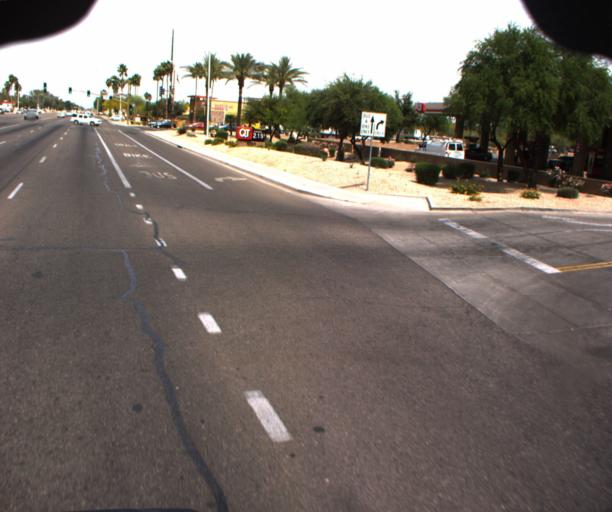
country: US
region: Arizona
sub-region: Maricopa County
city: San Carlos
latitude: 33.3341
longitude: -111.8416
